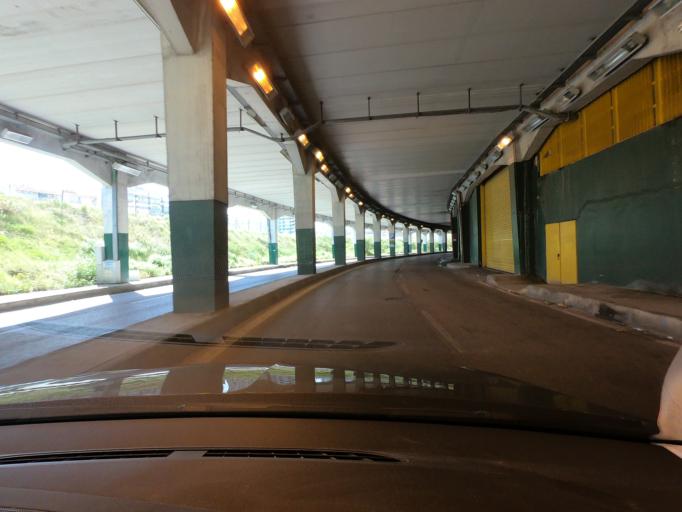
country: PT
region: Lisbon
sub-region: Odivelas
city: Olival do Basto
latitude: 38.7620
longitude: -9.1596
